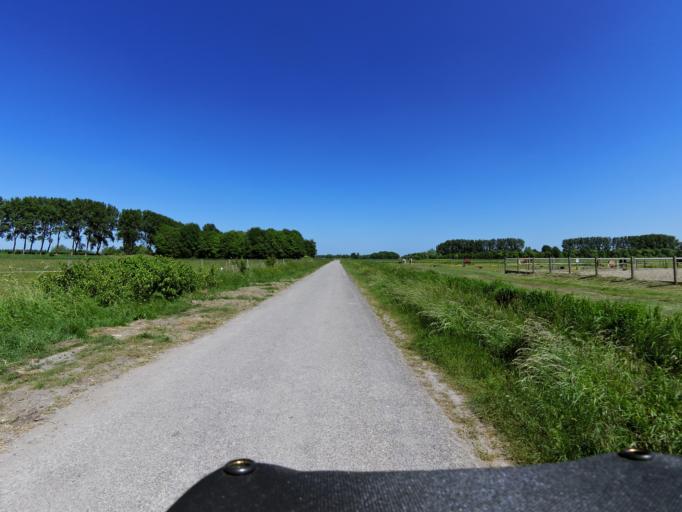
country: NL
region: South Holland
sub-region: Gemeente Hellevoetsluis
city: Nieuw-Helvoet
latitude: 51.8653
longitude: 4.0754
